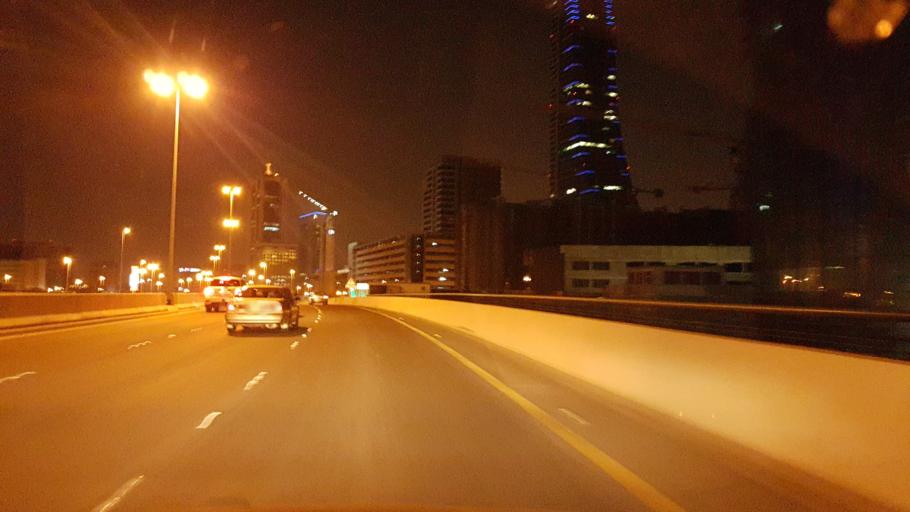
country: BH
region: Manama
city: Manama
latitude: 26.2420
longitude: 50.5745
